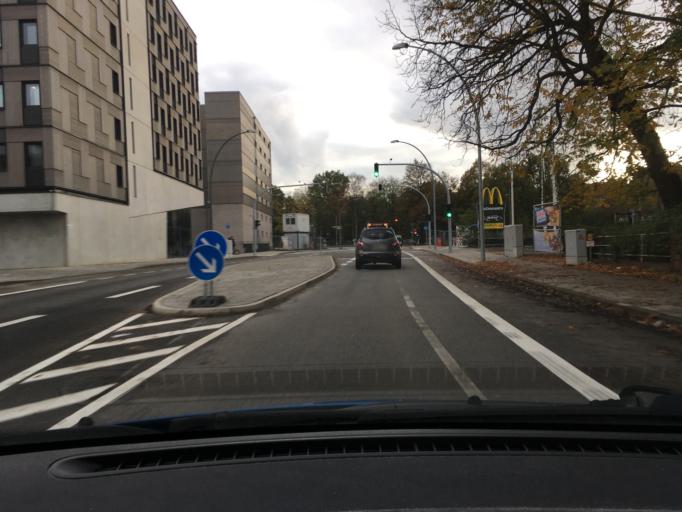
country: DE
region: Hamburg
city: Kleiner Grasbrook
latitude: 53.4997
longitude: 10.0006
